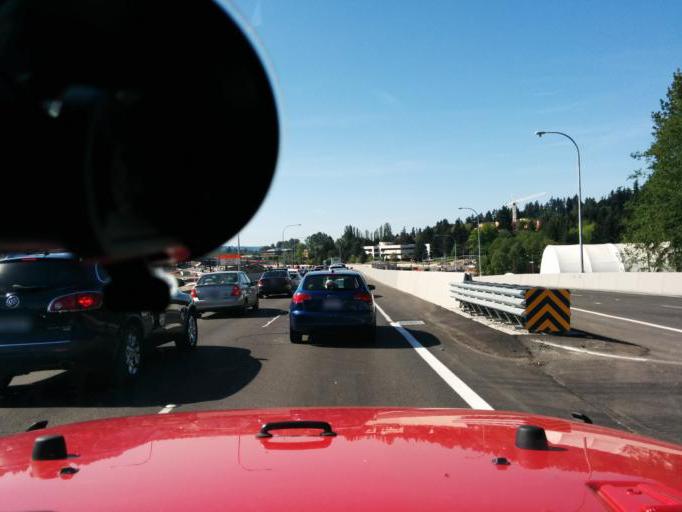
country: US
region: Washington
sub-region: King County
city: Yarrow Point
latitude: 47.6384
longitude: -122.1943
